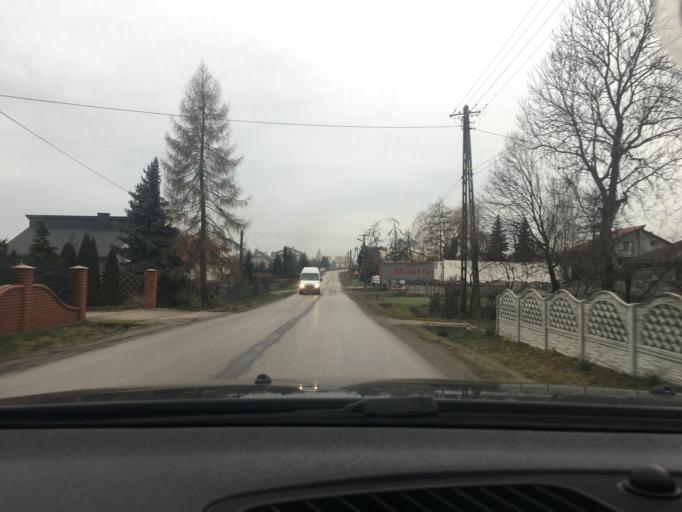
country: PL
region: Swietokrzyskie
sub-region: Powiat jedrzejowski
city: Jedrzejow
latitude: 50.6406
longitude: 20.3737
